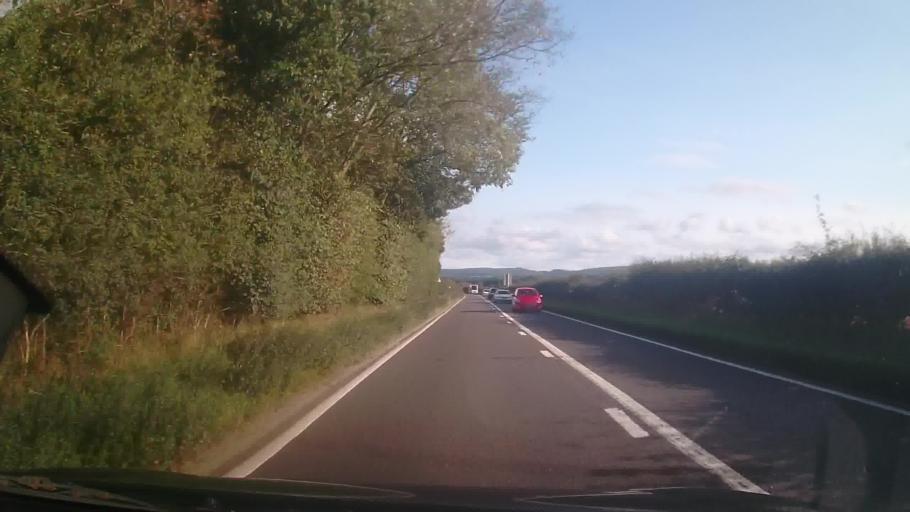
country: GB
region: England
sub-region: Shropshire
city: Bromfield
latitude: 52.4037
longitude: -2.8034
